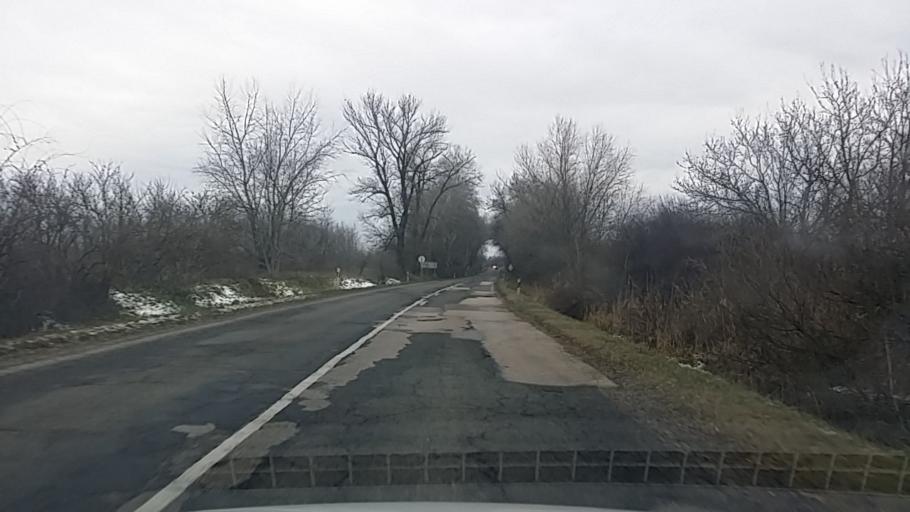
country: HU
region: Komarom-Esztergom
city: Csaszar
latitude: 47.4338
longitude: 18.1194
